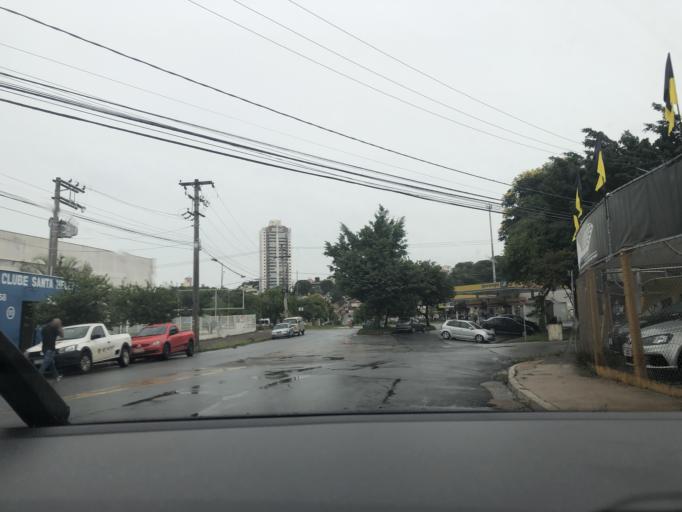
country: BR
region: Sao Paulo
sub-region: Jundiai
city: Jundiai
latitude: -23.2092
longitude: -46.8797
